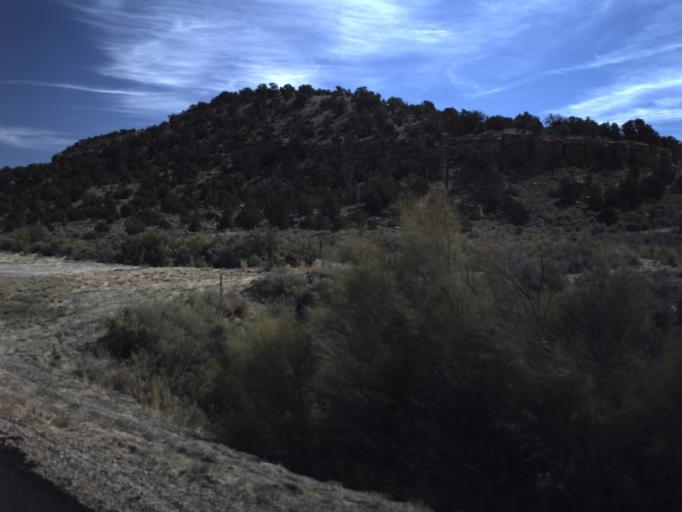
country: US
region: Utah
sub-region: Wayne County
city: Loa
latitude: 37.7702
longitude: -111.6631
